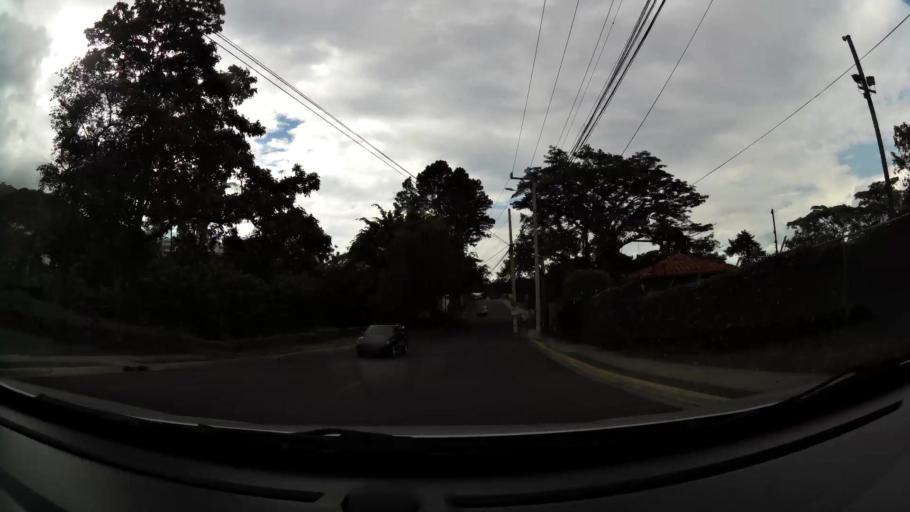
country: CR
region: San Jose
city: San Rafael
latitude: 9.9280
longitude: -84.1480
